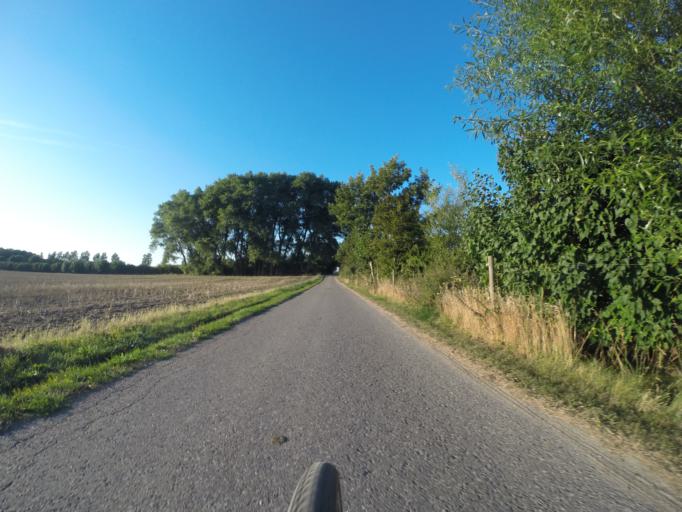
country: DK
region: Capital Region
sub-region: Ballerup Kommune
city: Ballerup
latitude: 55.7027
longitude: 12.3307
